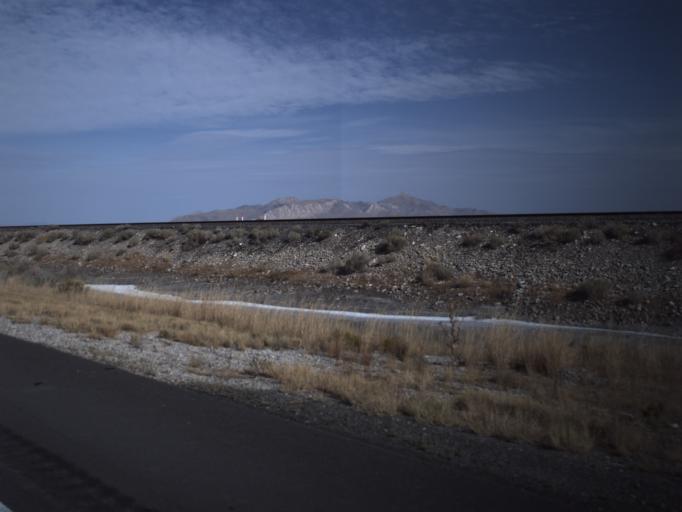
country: US
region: Utah
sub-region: Tooele County
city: Stansbury park
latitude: 40.6685
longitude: -112.3764
